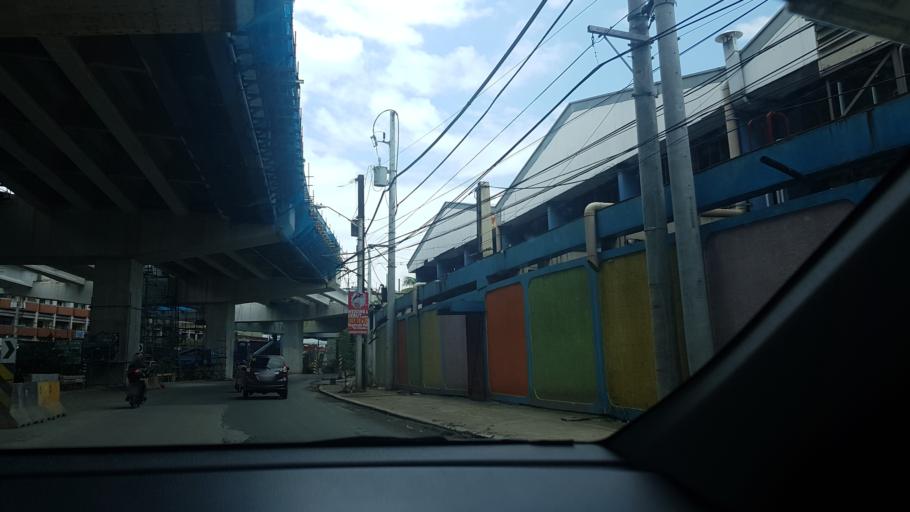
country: PH
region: Calabarzon
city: Del Monte
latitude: 14.6377
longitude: 121.0082
